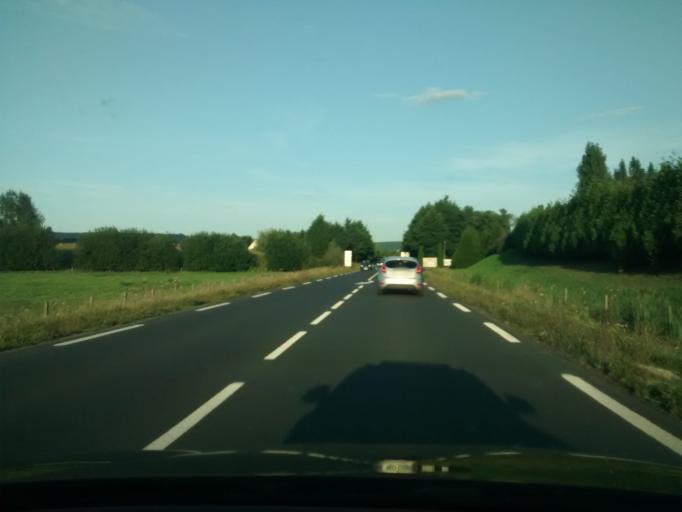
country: FR
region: Lower Normandy
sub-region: Departement du Calvados
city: Touques
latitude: 49.3279
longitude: 0.0799
